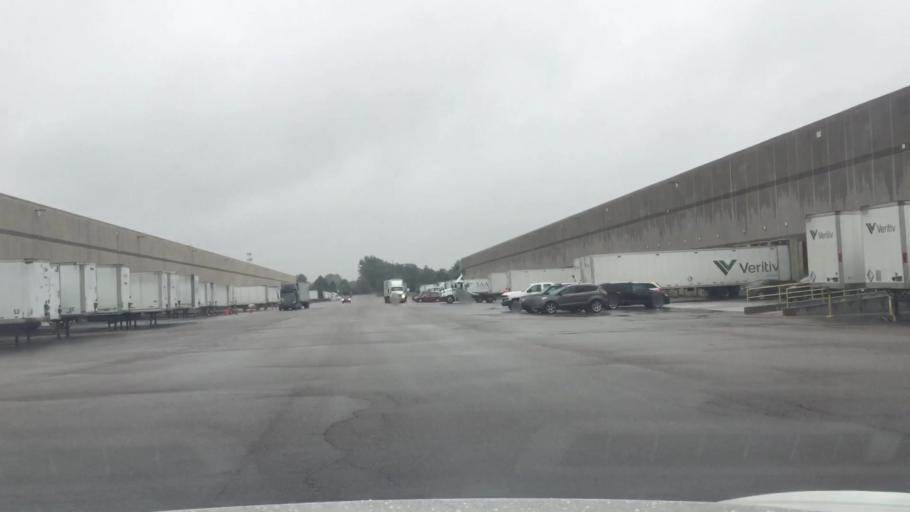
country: US
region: Michigan
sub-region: Wayne County
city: Livonia
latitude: 42.3780
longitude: -83.3256
